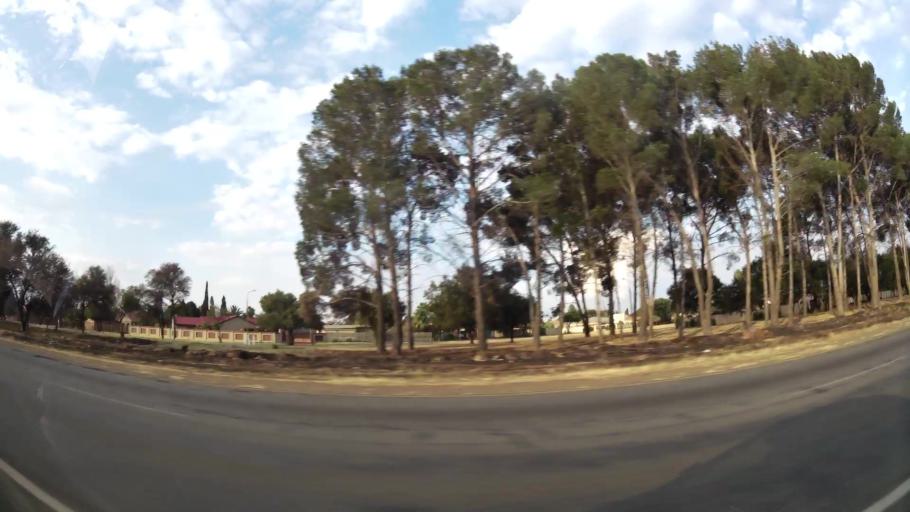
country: ZA
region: Gauteng
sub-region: Sedibeng District Municipality
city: Vanderbijlpark
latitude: -26.7166
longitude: 27.8182
